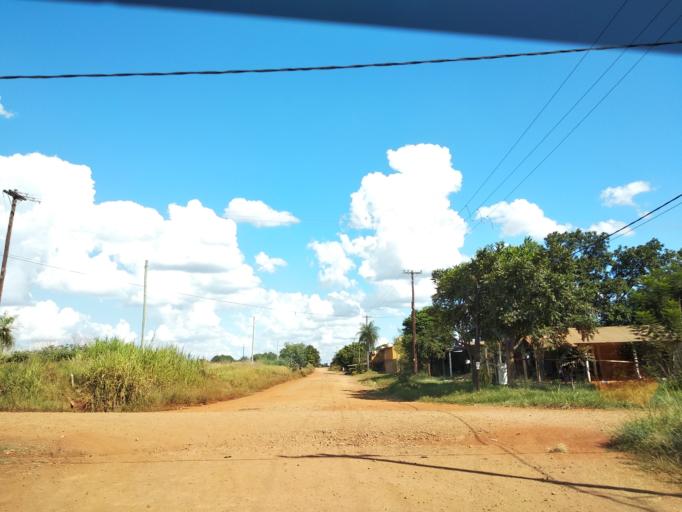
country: AR
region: Misiones
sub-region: Departamento de Capital
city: Posadas
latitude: -27.3792
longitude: -55.9448
